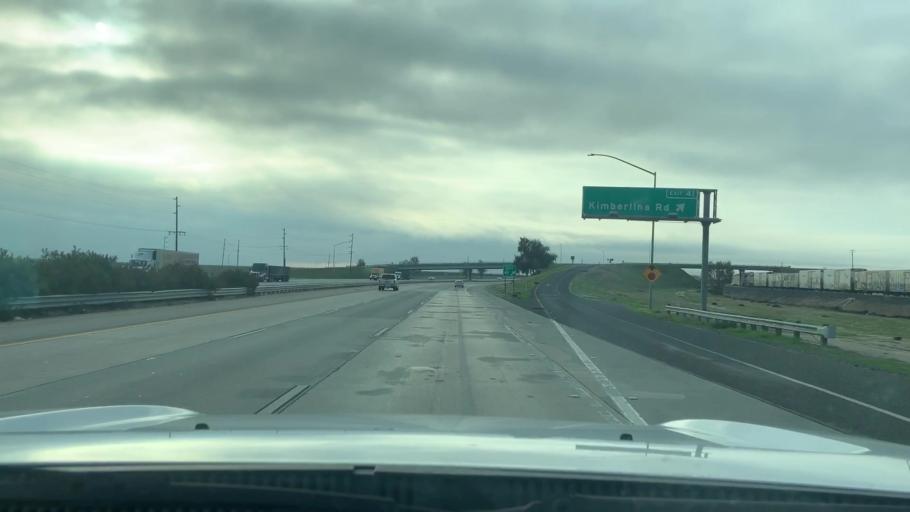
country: US
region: California
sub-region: Kern County
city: Shafter
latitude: 35.5616
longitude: -119.1988
